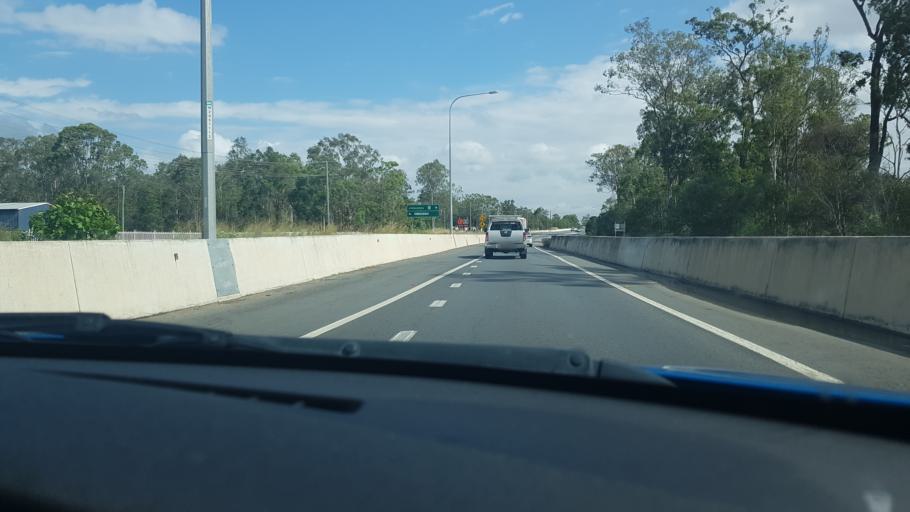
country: AU
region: Queensland
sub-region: Logan
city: North Maclean
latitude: -27.7651
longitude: 153.0183
